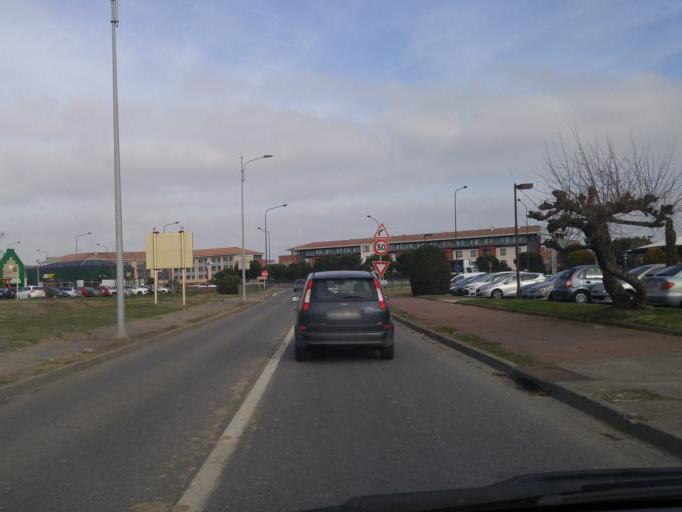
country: FR
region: Midi-Pyrenees
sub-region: Departement de la Haute-Garonne
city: Blagnac
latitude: 43.6374
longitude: 1.3756
